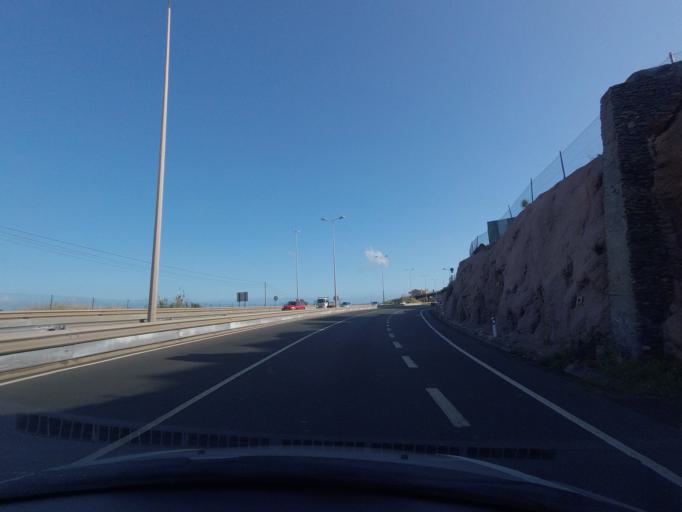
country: PT
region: Madeira
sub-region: Santa Cruz
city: Santa Cruz
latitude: 32.6700
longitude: -16.8035
